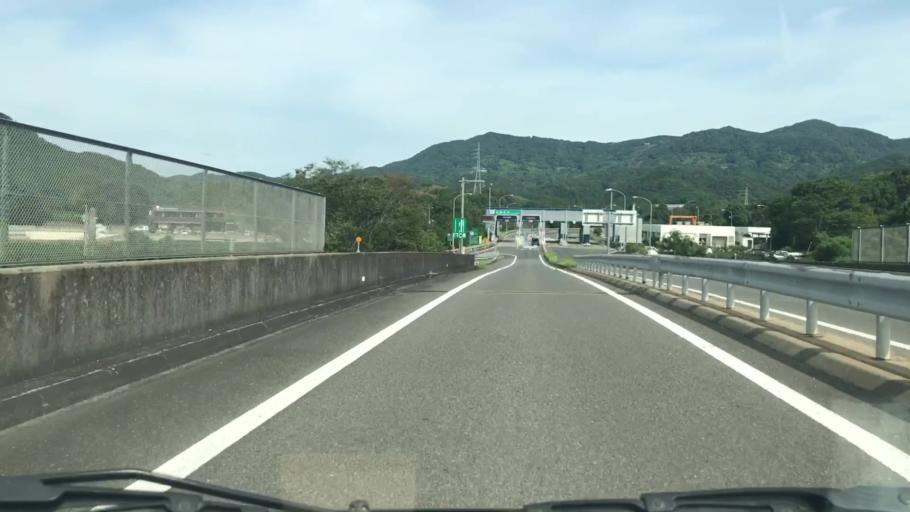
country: JP
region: Saga Prefecture
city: Takeocho-takeo
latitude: 33.2153
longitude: 130.0503
